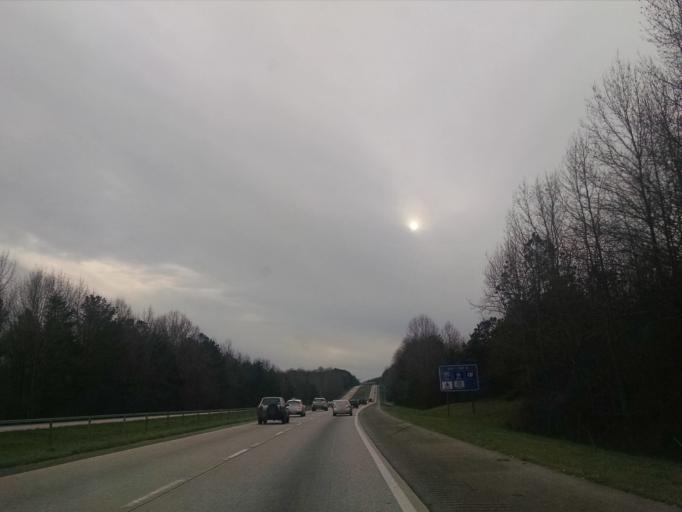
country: US
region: Georgia
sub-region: Hall County
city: Flowery Branch
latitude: 34.1555
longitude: -83.9313
